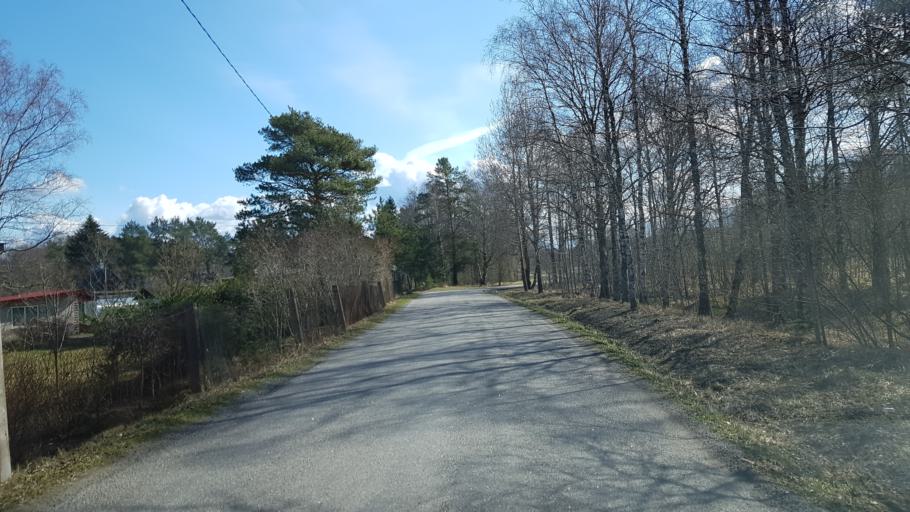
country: EE
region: Ida-Virumaa
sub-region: Narva-Joesuu linn
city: Narva-Joesuu
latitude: 59.4132
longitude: 28.0642
